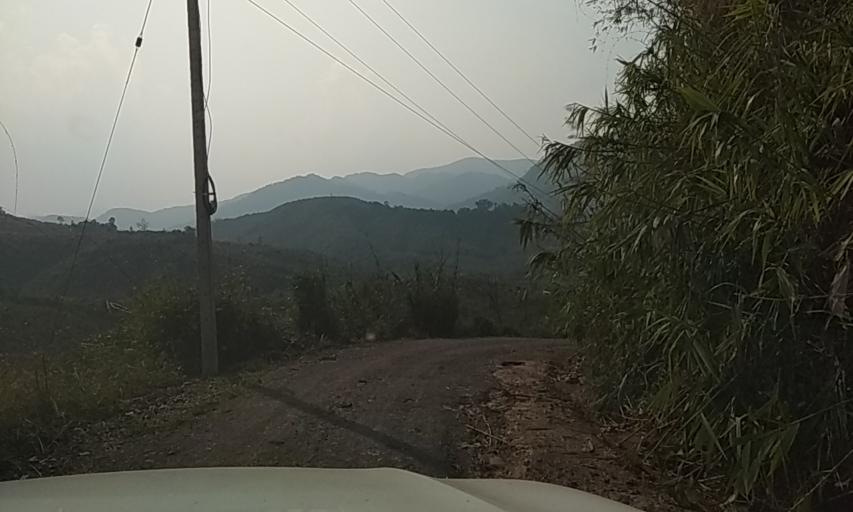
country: LA
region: Louangphabang
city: Louangphabang
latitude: 20.0386
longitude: 101.8155
